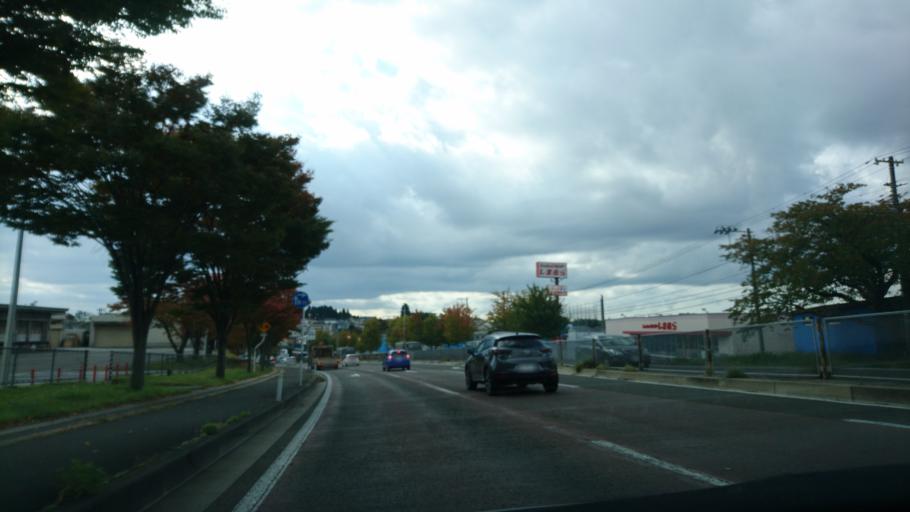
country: JP
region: Miyagi
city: Tomiya
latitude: 38.3552
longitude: 140.8707
